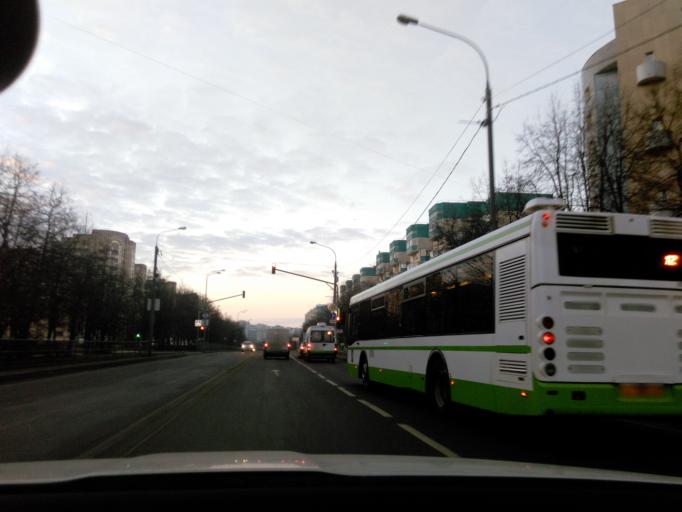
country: RU
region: Moskovskaya
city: Mendeleyevo
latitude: 56.0064
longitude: 37.2036
